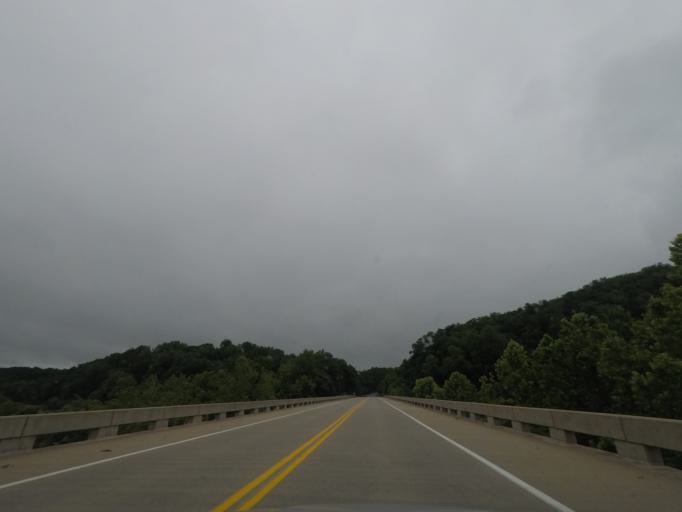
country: US
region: Virginia
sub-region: Fluvanna County
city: Weber City
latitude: 37.7125
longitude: -78.3021
